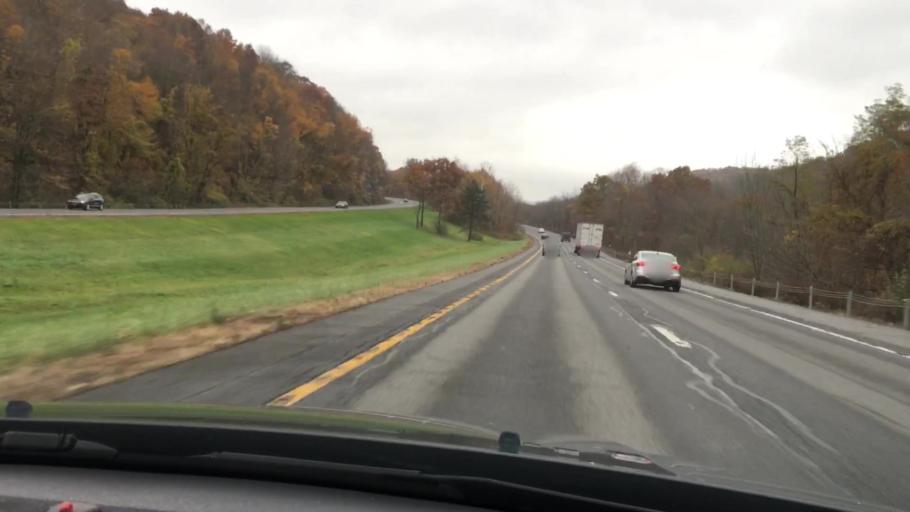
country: US
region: New York
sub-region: Putnam County
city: Lake Carmel
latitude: 41.4809
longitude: -73.6532
